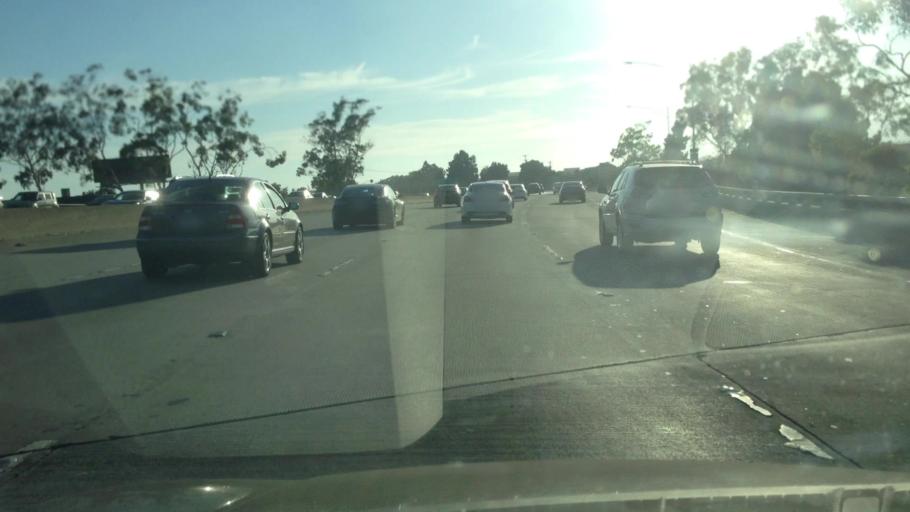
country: US
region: California
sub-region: Los Angeles County
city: Westwood, Los Angeles
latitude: 34.0291
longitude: -118.4522
